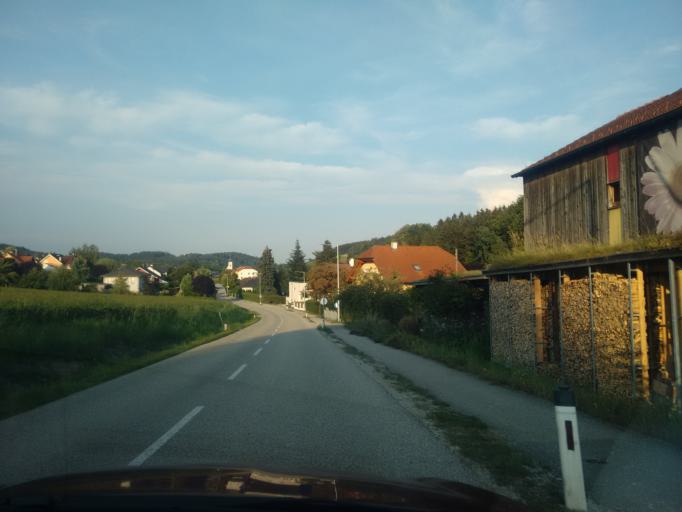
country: AT
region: Upper Austria
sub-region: Wels-Land
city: Offenhausen
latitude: 48.1561
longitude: 13.8259
